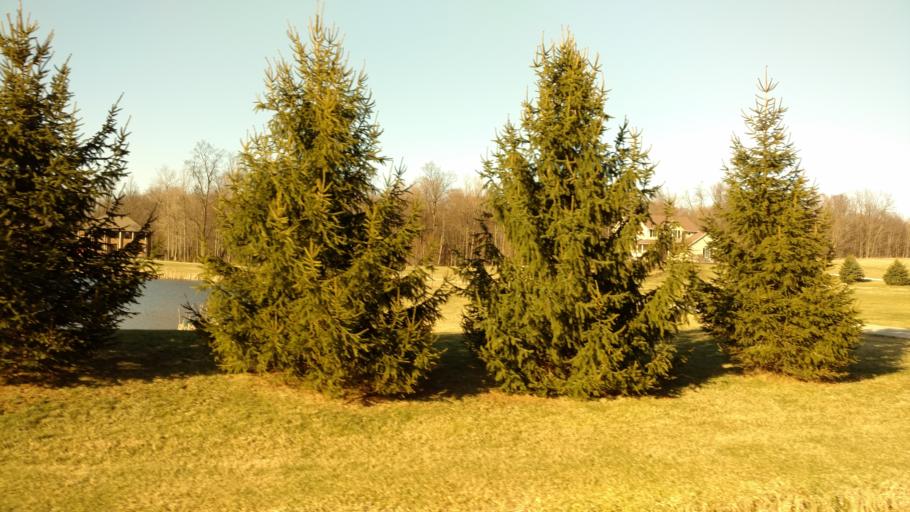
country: US
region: Ohio
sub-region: Richland County
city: Ontario
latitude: 40.7300
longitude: -82.6264
